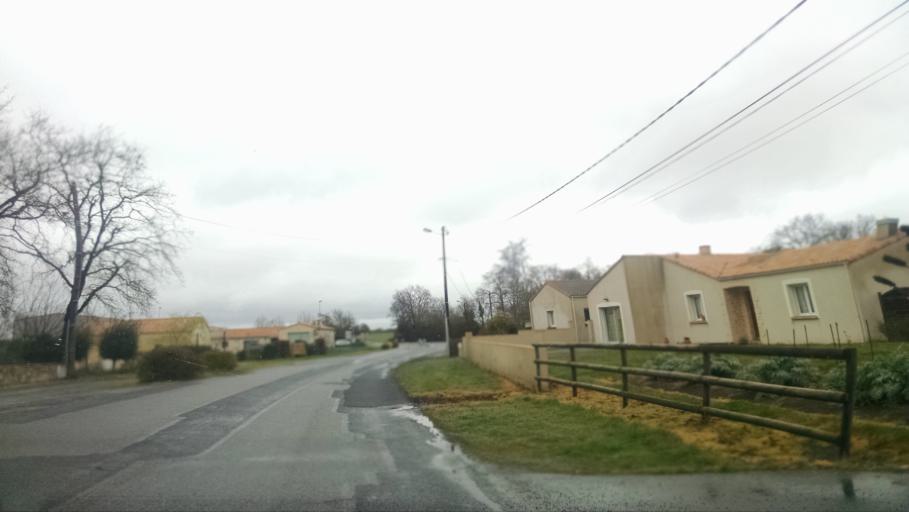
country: FR
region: Pays de la Loire
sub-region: Departement de la Loire-Atlantique
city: Maisdon-sur-Sevre
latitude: 47.1011
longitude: -1.3809
